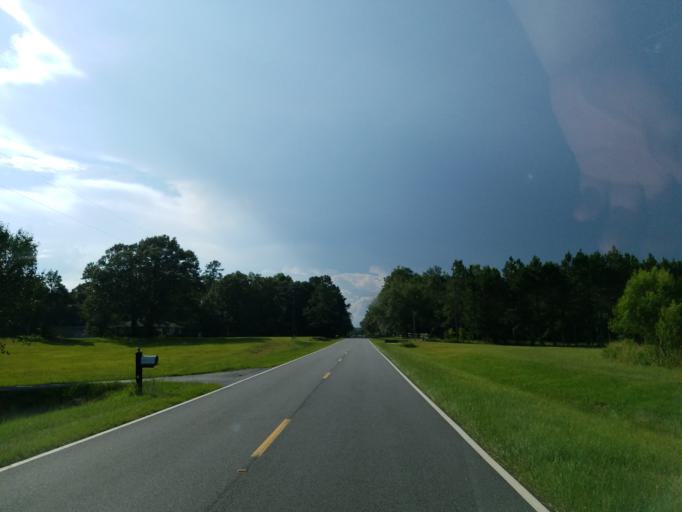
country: US
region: Georgia
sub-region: Lowndes County
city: Hahira
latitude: 31.0239
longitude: -83.4374
